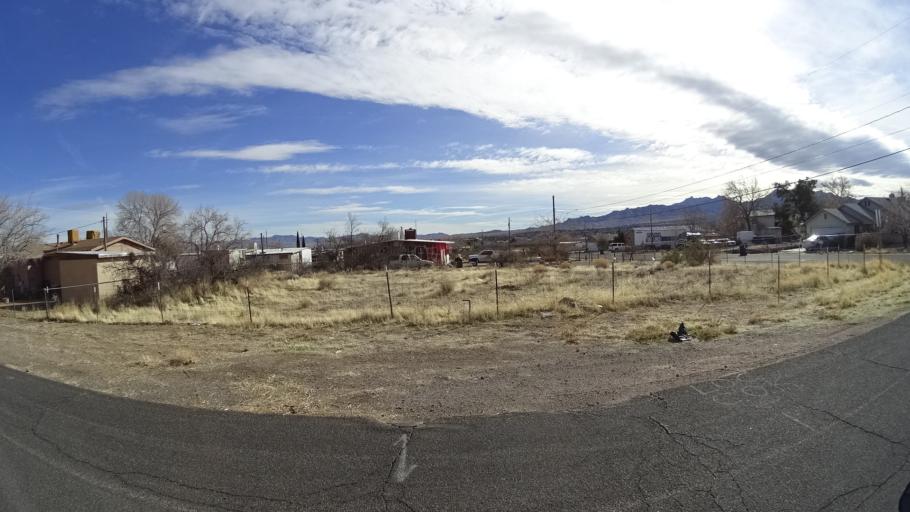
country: US
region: Arizona
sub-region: Mohave County
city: Kingman
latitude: 35.2159
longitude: -114.0490
